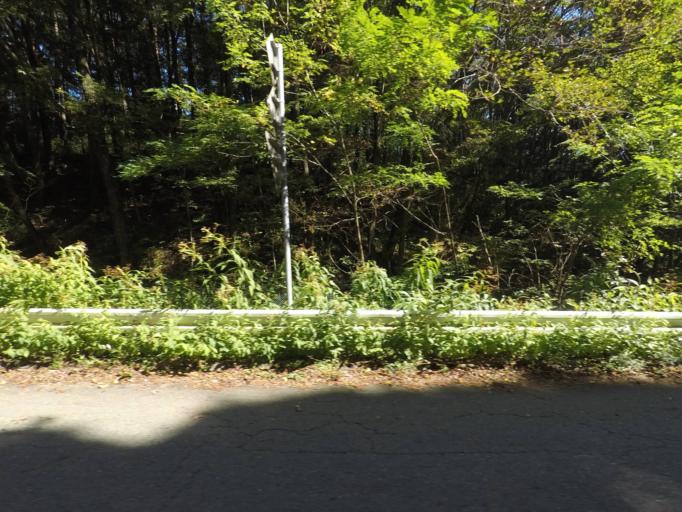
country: JP
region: Nagano
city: Tatsuno
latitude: 35.9744
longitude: 137.7472
